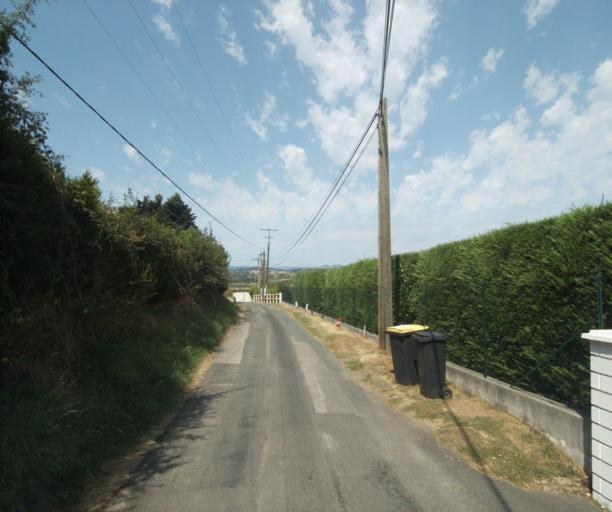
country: FR
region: Rhone-Alpes
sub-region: Departement du Rhone
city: Lentilly
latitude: 45.8463
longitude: 4.6523
